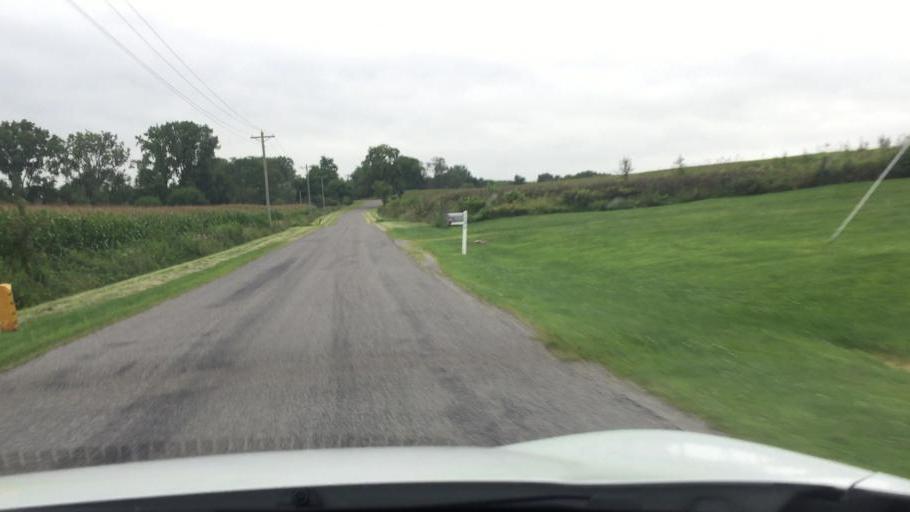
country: US
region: Ohio
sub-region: Champaign County
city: Mechanicsburg
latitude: 40.0602
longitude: -83.5726
